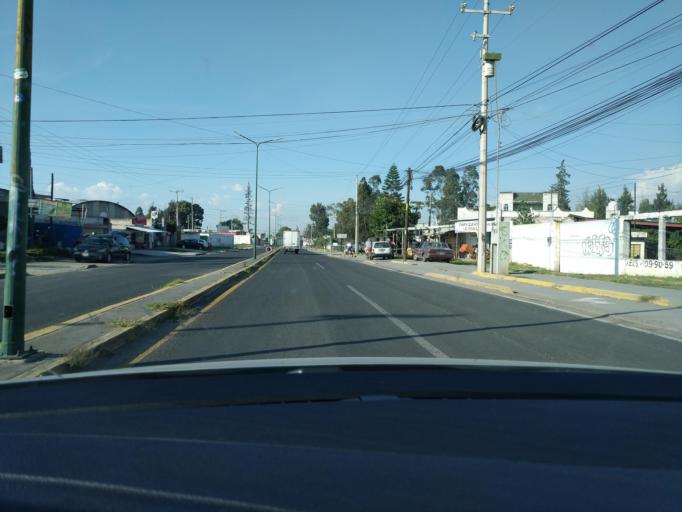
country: MX
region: Puebla
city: San Andres Cholula
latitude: 19.0421
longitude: -98.3152
